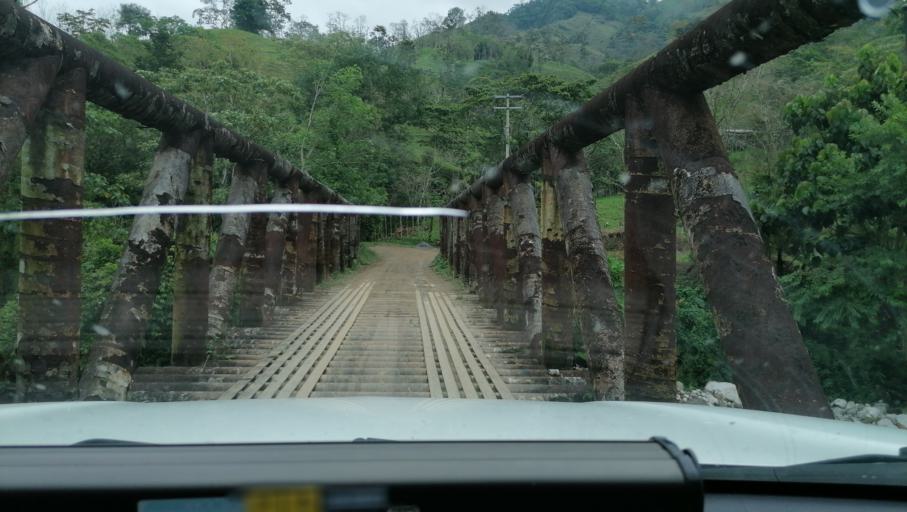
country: MX
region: Chiapas
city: Ocotepec
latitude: 17.3165
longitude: -93.1357
